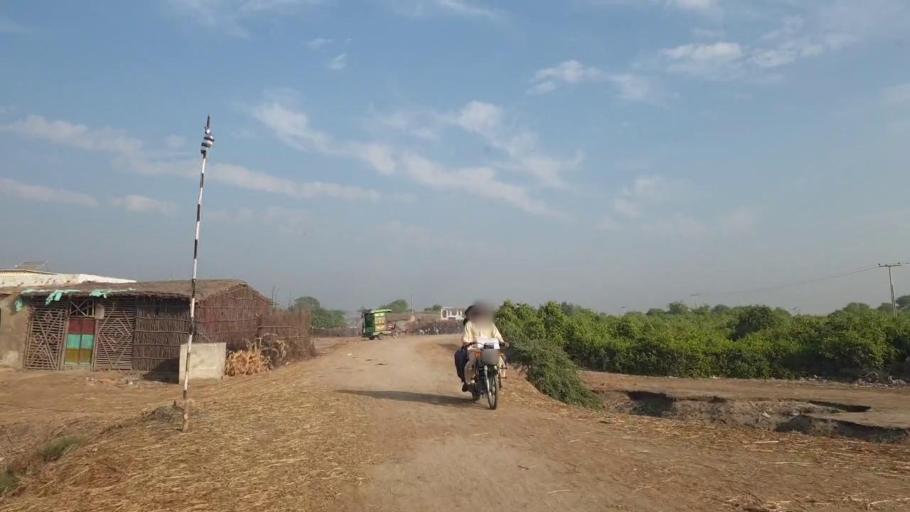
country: PK
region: Sindh
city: Tando Bago
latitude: 24.8245
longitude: 68.9741
